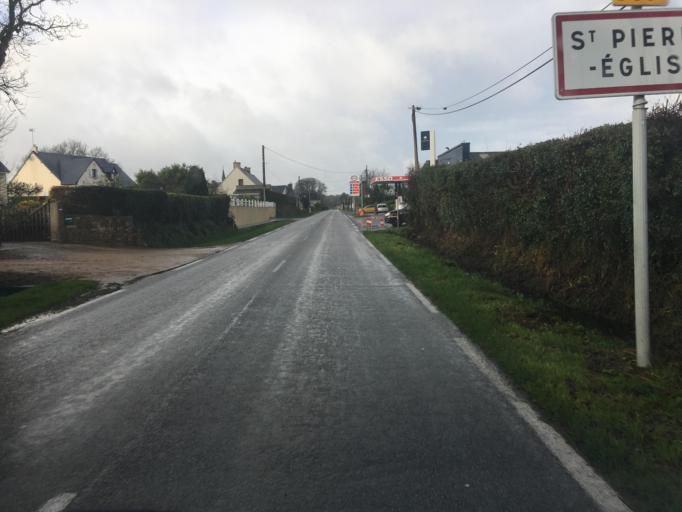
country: FR
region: Lower Normandy
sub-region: Departement de la Manche
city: Saint-Pierre-Eglise
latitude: 49.6674
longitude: -1.3902
